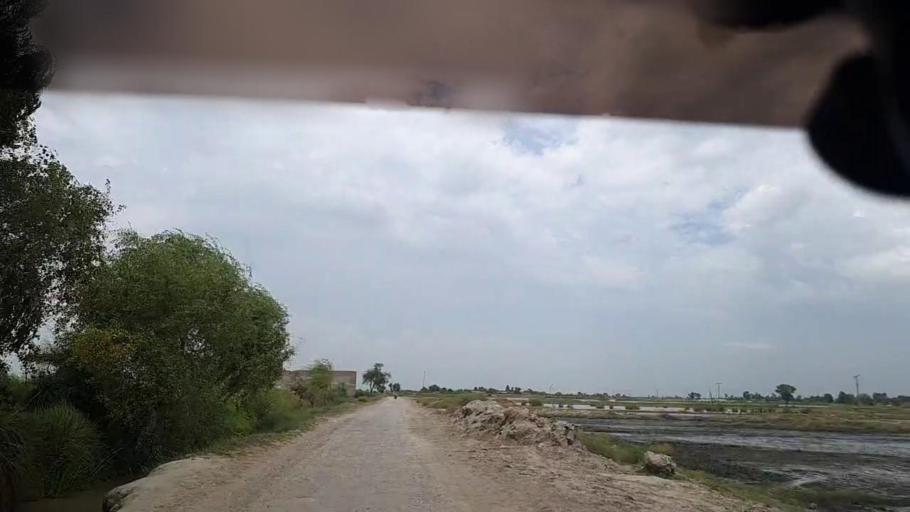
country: PK
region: Sindh
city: Ghauspur
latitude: 28.1118
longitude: 68.9858
